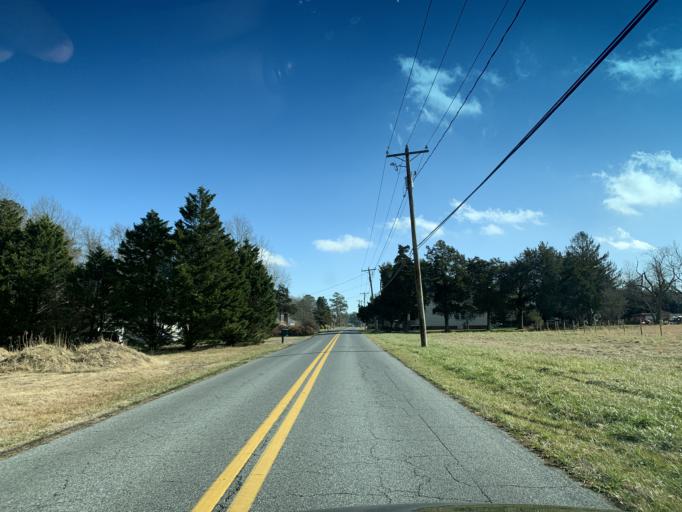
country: US
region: Delaware
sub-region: Sussex County
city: Selbyville
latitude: 38.4551
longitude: -75.2028
